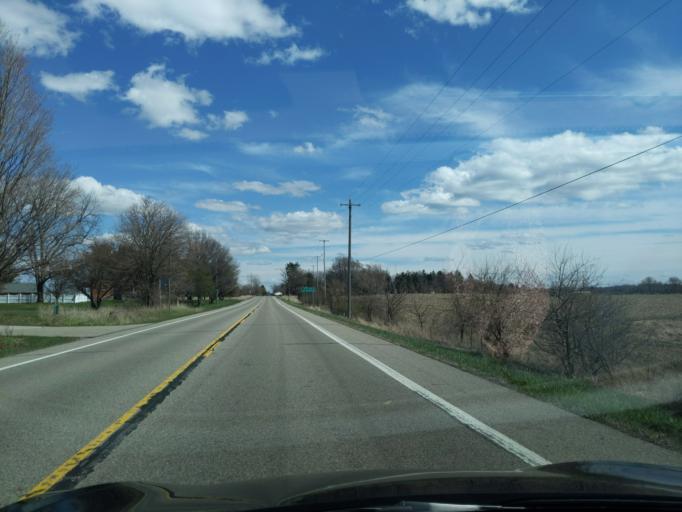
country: US
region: Michigan
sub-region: Ingham County
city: Mason
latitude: 42.5759
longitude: -84.4218
